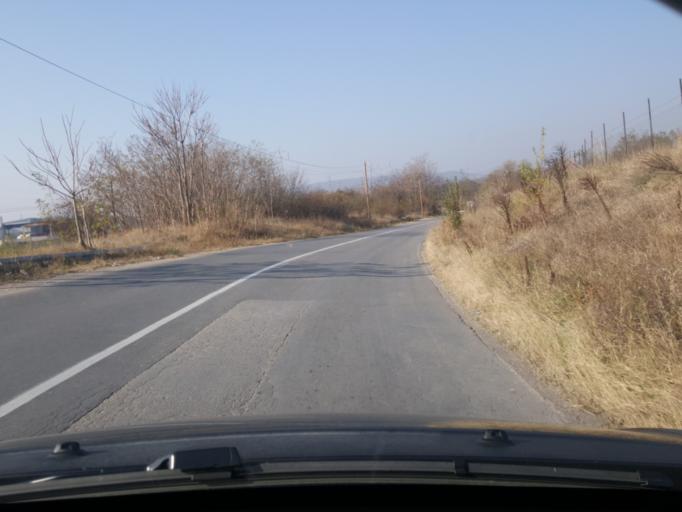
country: RS
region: Central Serbia
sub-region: Nisavski Okrug
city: Niska Banja
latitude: 43.3251
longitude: 21.9704
